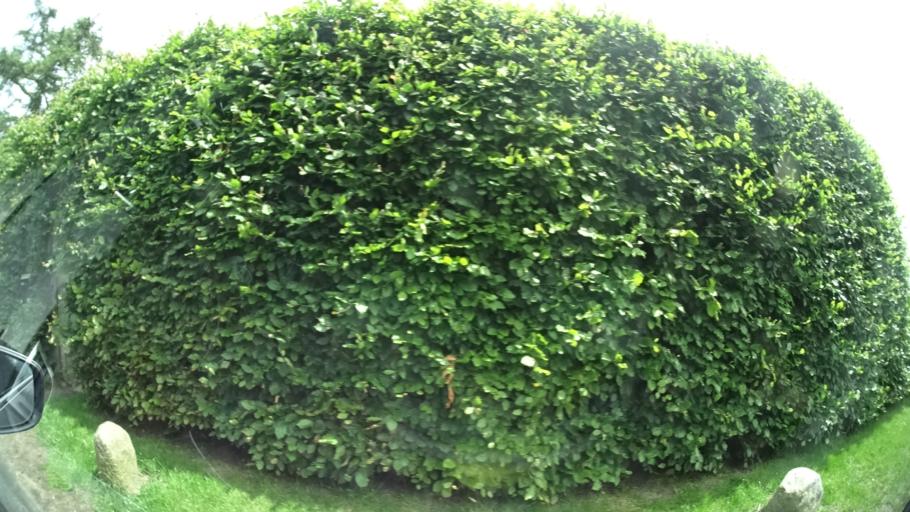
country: DK
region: Central Jutland
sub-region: Syddjurs Kommune
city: Ronde
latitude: 56.2955
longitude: 10.4103
